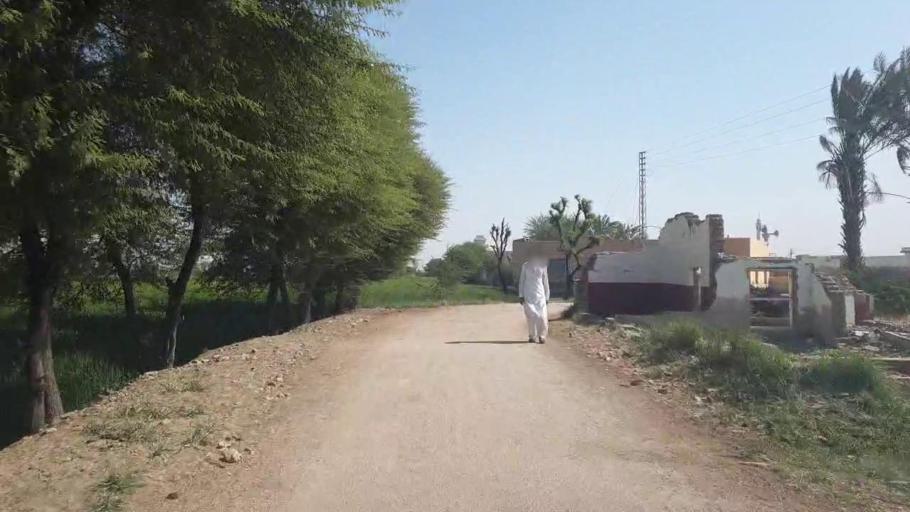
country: PK
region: Sindh
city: Umarkot
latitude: 25.3084
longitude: 69.6138
